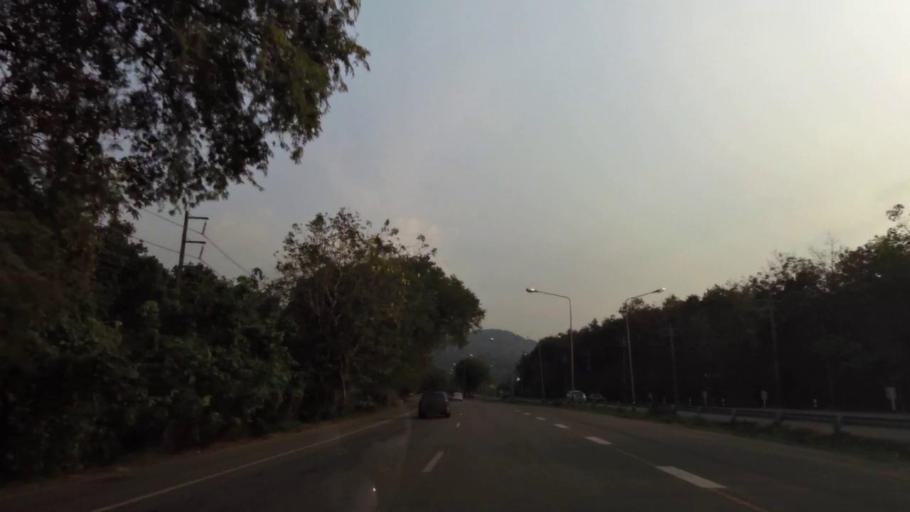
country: TH
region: Chanthaburi
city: Chanthaburi
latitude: 12.5766
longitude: 102.1605
